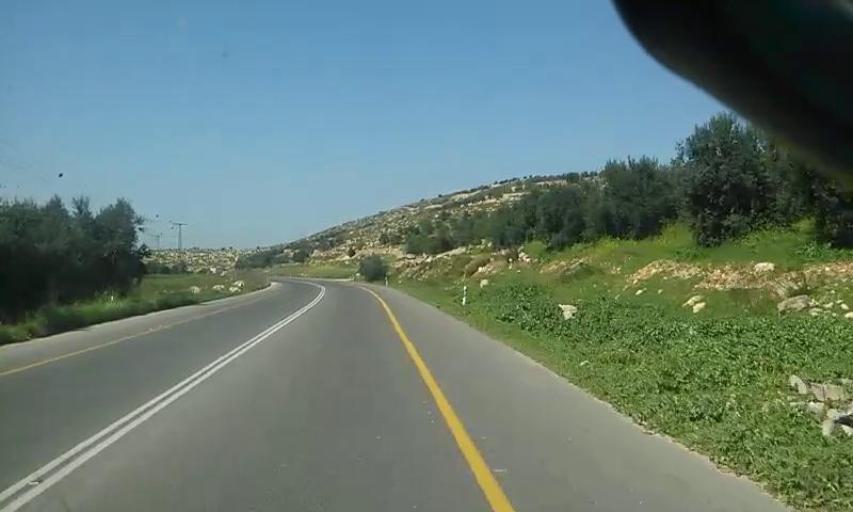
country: PS
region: West Bank
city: Idhna
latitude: 31.5780
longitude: 34.9792
